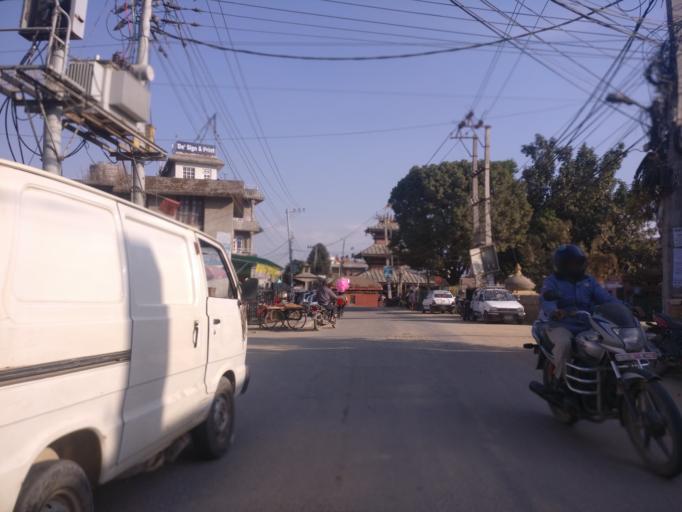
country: NP
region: Central Region
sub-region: Bagmati Zone
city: Patan
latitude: 27.6724
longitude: 85.3353
